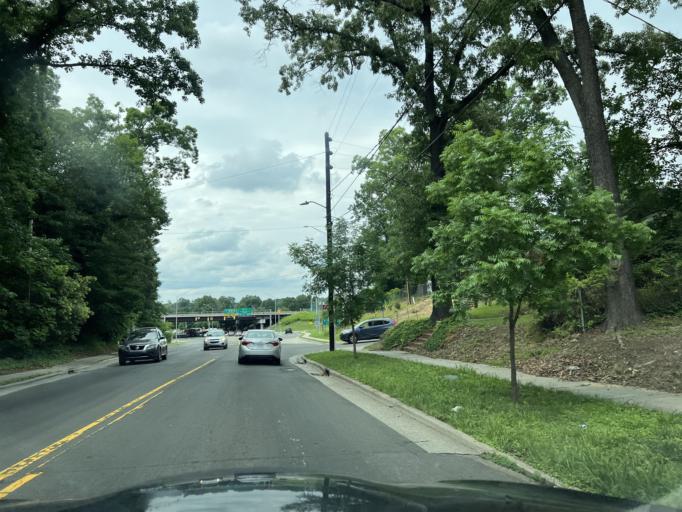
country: US
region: North Carolina
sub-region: Durham County
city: Durham
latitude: 36.0121
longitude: -78.8867
